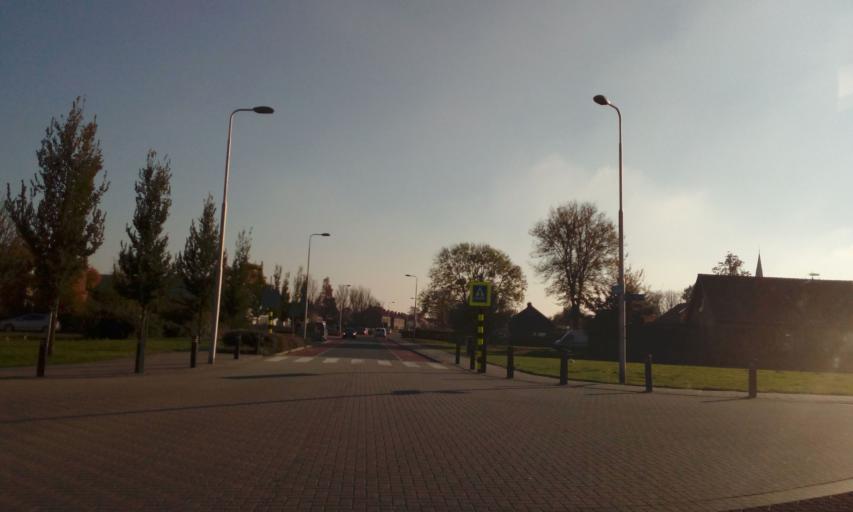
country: NL
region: South Holland
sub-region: Gemeente Lansingerland
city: Bleiswijk
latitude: 52.0154
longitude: 4.5812
